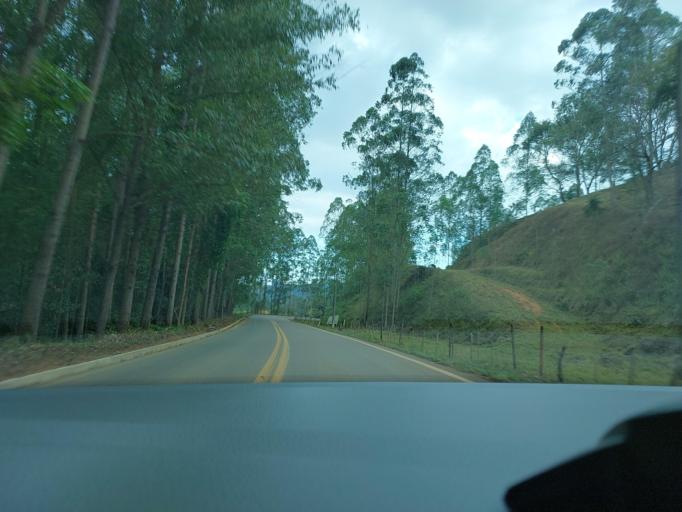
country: BR
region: Minas Gerais
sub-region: Mirai
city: Mirai
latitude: -20.9927
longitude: -42.5699
